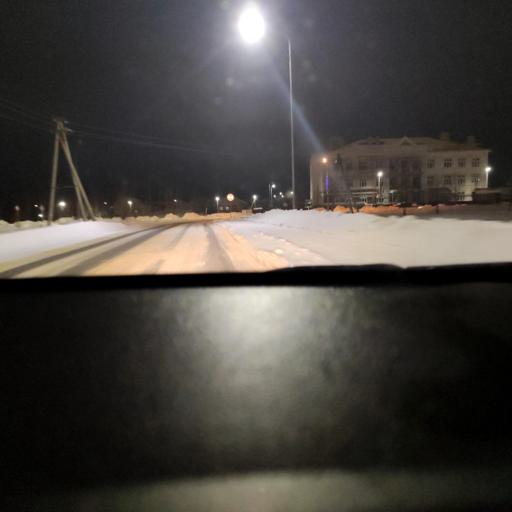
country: RU
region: Tatarstan
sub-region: Chistopol'skiy Rayon
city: Chistopol'
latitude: 55.3613
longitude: 50.5825
